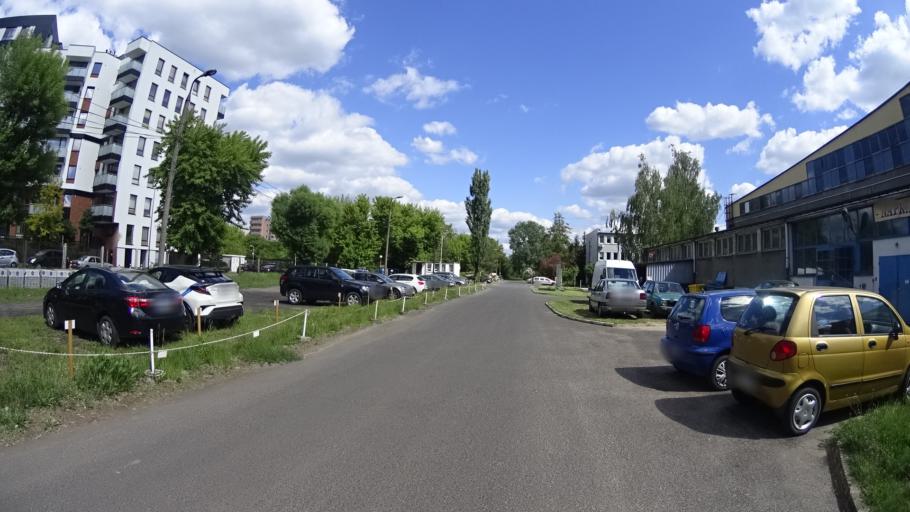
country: PL
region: Masovian Voivodeship
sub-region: Warszawa
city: Bemowo
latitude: 52.2723
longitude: 20.9138
